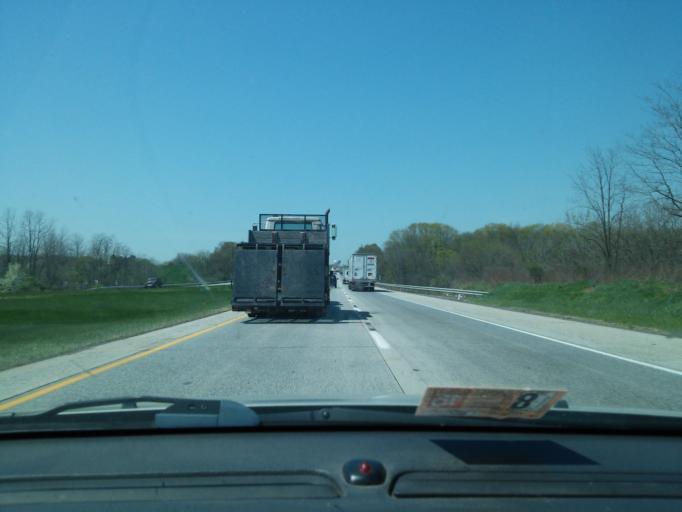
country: US
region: Pennsylvania
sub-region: Lebanon County
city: Fredericksburg
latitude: 40.4540
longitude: -76.3895
